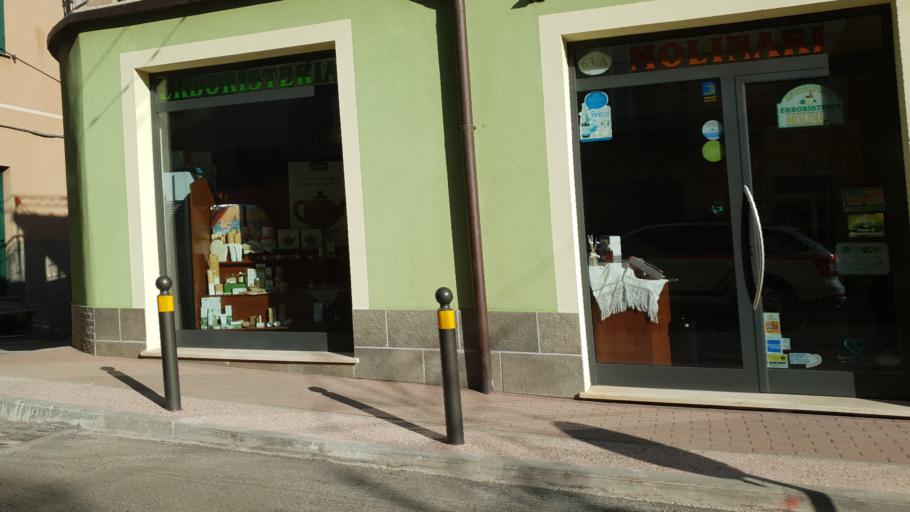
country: IT
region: Liguria
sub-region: Provincia di Savona
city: Valleggia
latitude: 44.2812
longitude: 8.4311
